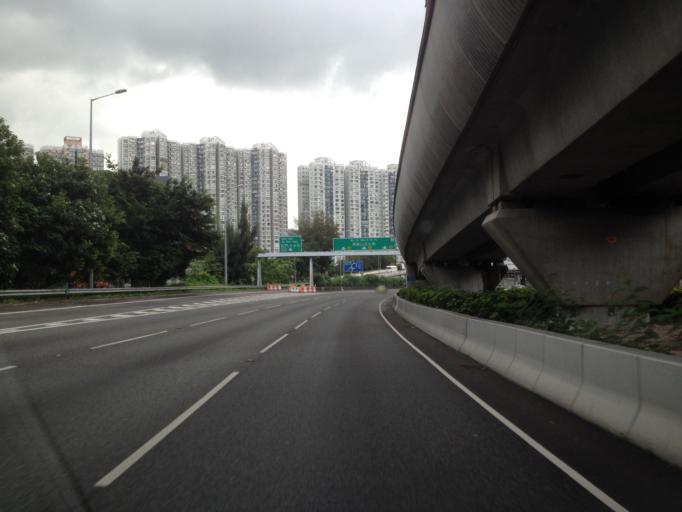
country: HK
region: Sha Tin
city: Sha Tin
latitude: 22.3910
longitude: 114.2097
